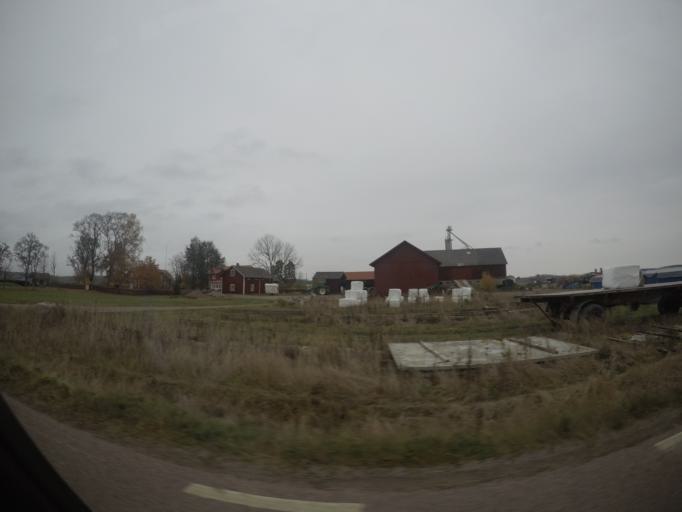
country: SE
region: Vaestmanland
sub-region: Kopings Kommun
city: Koping
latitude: 59.5583
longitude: 16.0962
